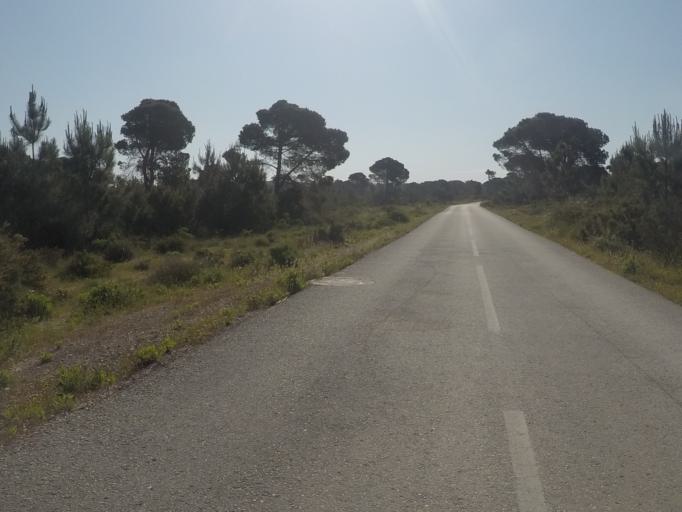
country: PT
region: Setubal
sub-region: Sesimbra
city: Sesimbra
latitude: 38.4899
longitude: -9.1718
